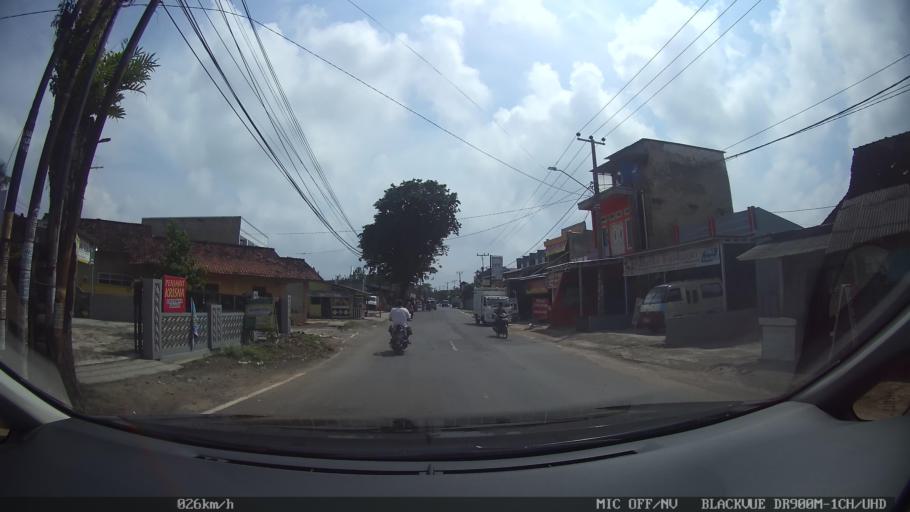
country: ID
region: Lampung
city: Kedaton
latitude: -5.3502
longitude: 105.2927
